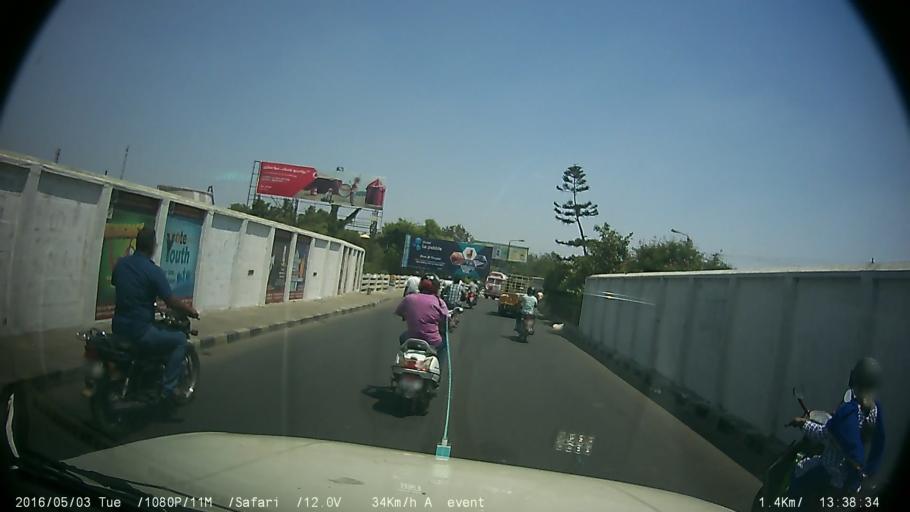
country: IN
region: Tamil Nadu
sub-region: Tiruppur
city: Tiruppur
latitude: 11.1091
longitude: 77.3418
